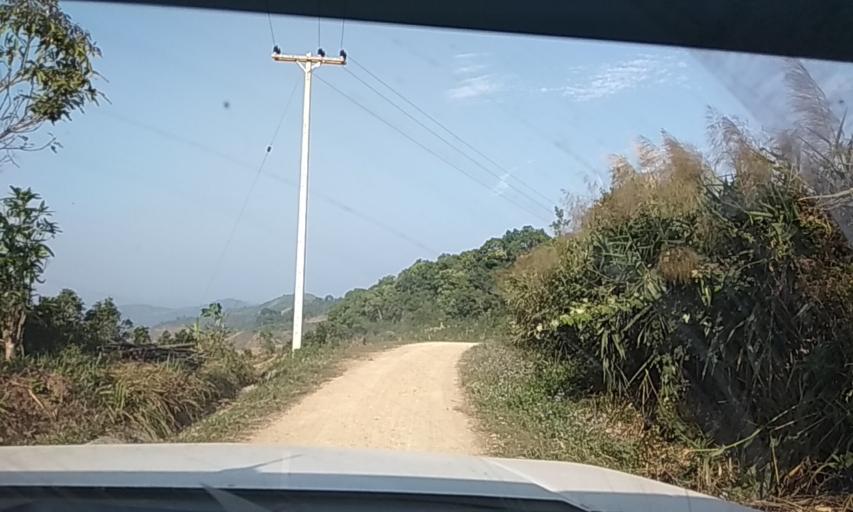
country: LA
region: Phongsali
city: Phongsali
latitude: 21.6594
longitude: 102.1700
